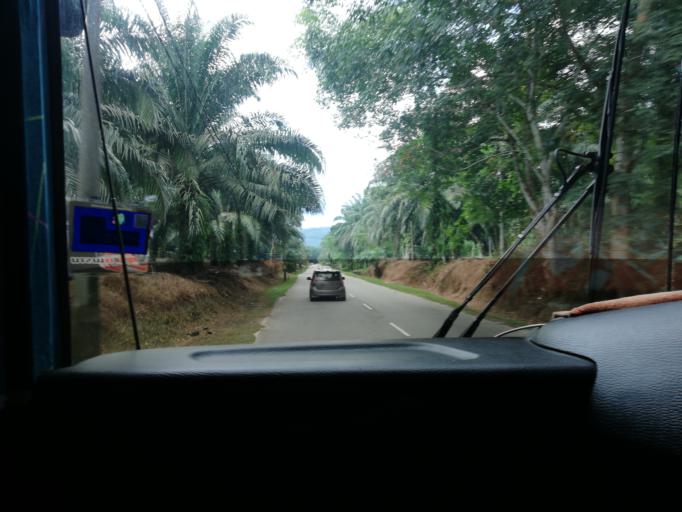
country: MY
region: Kedah
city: Kulim
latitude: 5.2347
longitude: 100.6032
